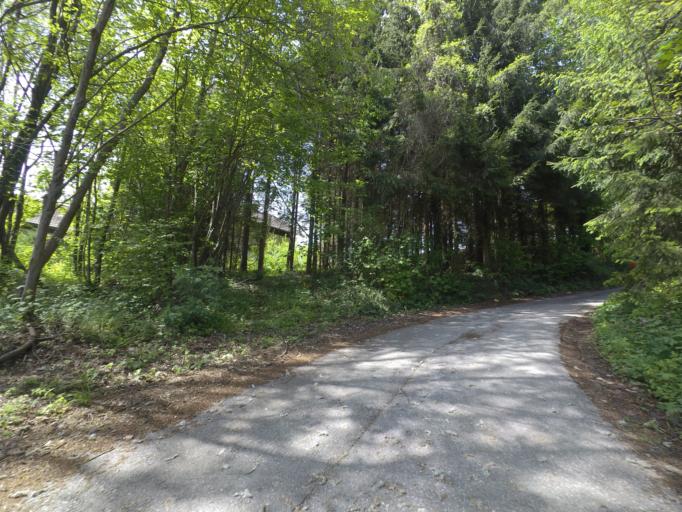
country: AT
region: Salzburg
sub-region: Politischer Bezirk Salzburg-Umgebung
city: Berndorf bei Salzburg
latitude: 47.9848
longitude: 13.0773
